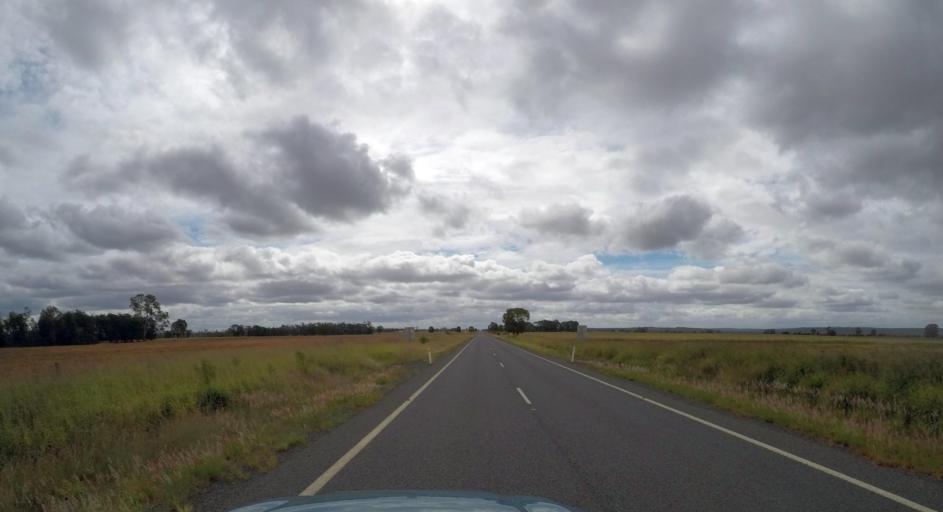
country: AU
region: Queensland
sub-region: South Burnett
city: Kingaroy
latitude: -26.3891
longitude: 151.2446
